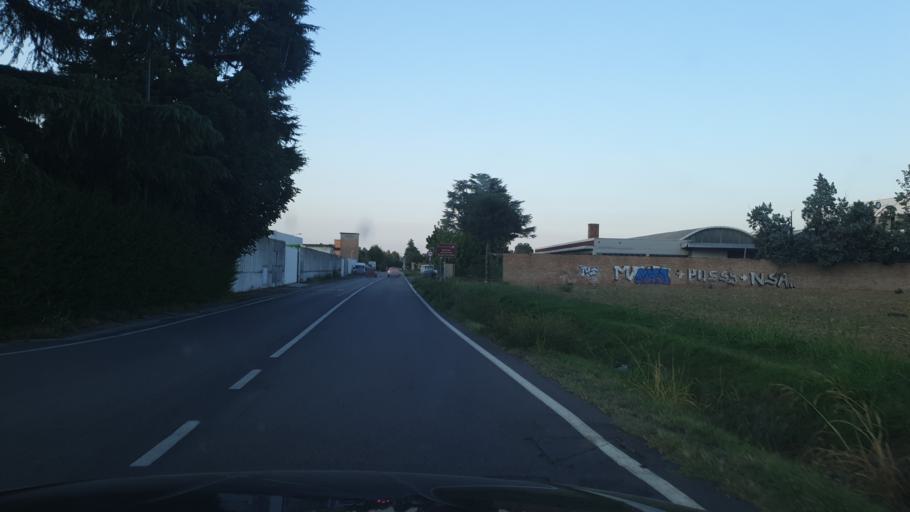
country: IT
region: Emilia-Romagna
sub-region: Provincia di Bologna
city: Quarto Inferiore
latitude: 44.5425
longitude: 11.3951
